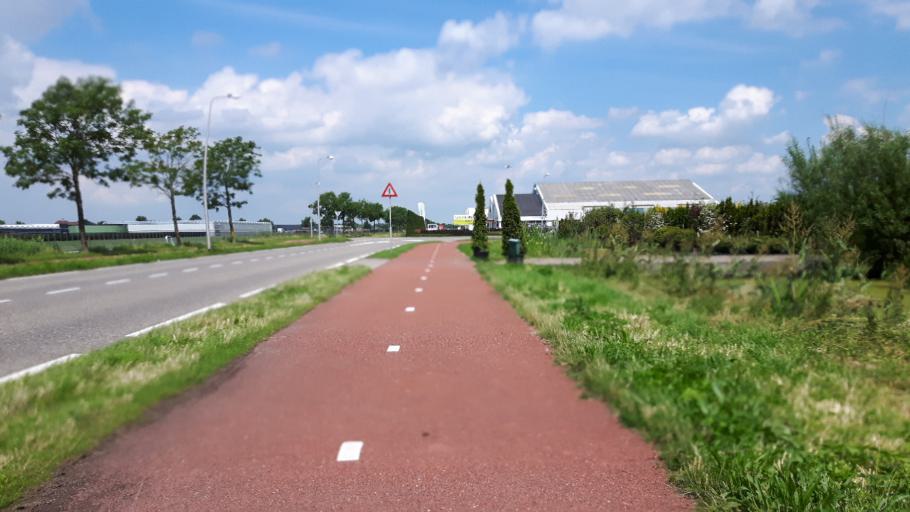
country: NL
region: South Holland
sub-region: Gemeente Boskoop
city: Boskoop
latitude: 52.0920
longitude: 4.6841
